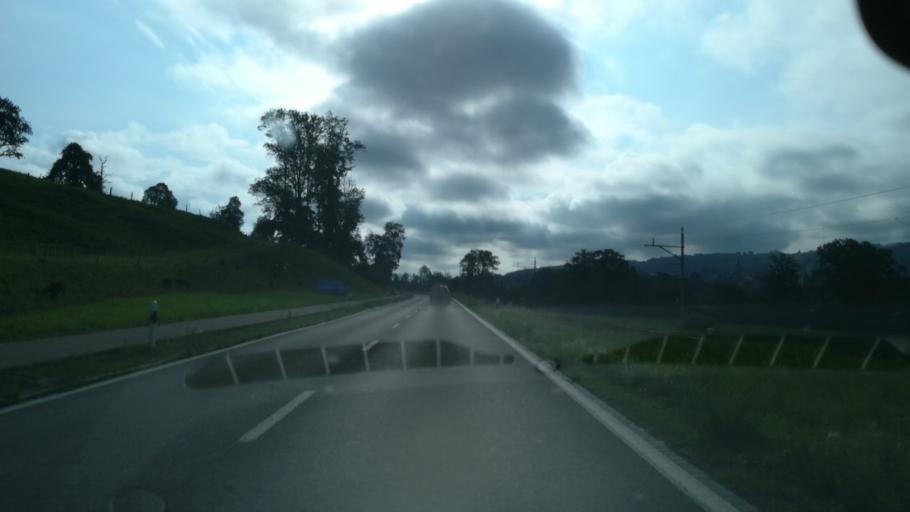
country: CH
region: Saint Gallen
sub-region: Wahlkreis Wil
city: Niederburen
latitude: 47.4975
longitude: 9.2229
